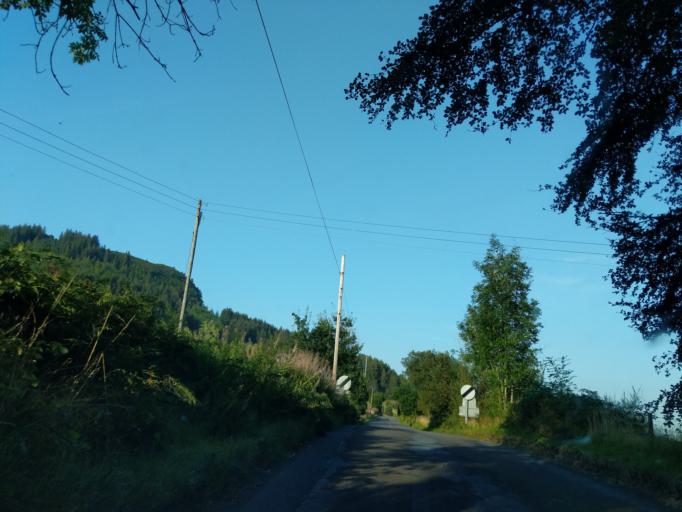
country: GB
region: Scotland
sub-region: Stirling
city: Balfron
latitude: 56.1736
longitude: -4.3616
